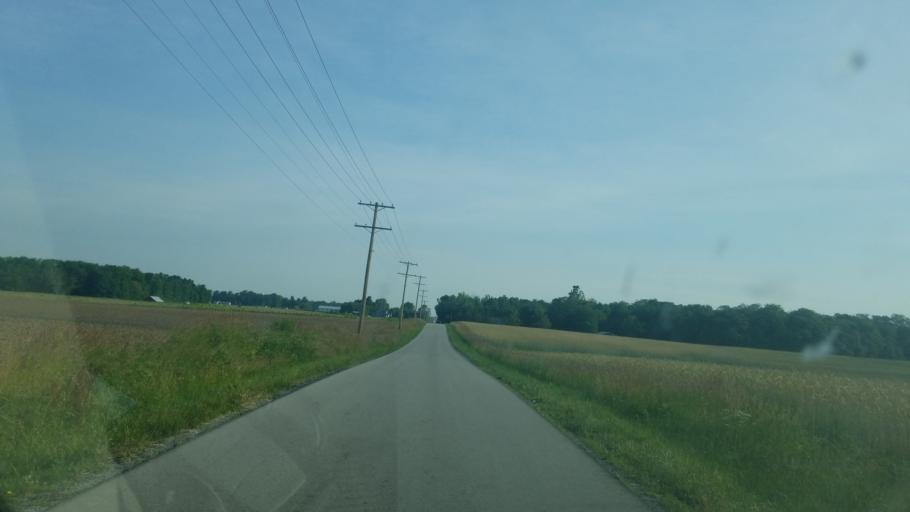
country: US
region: Ohio
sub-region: Hancock County
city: Arlington
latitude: 40.8590
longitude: -83.6702
